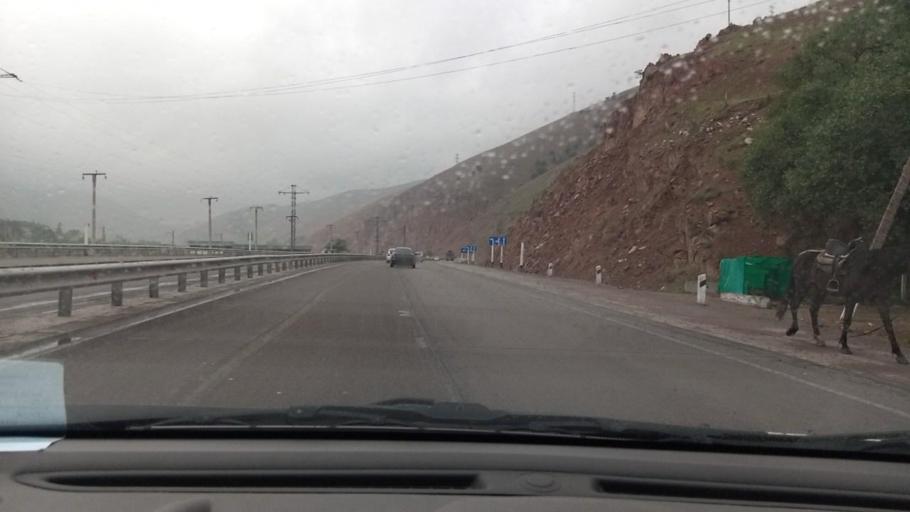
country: UZ
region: Toshkent
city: Angren
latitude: 41.1513
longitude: 70.4321
